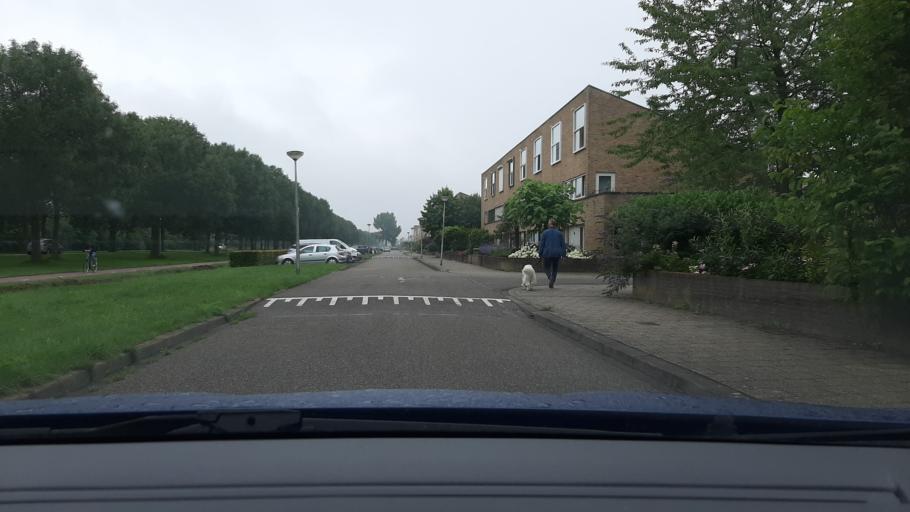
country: NL
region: Flevoland
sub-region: Gemeente Zeewolde
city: Zeewolde
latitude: 52.3428
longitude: 5.5198
